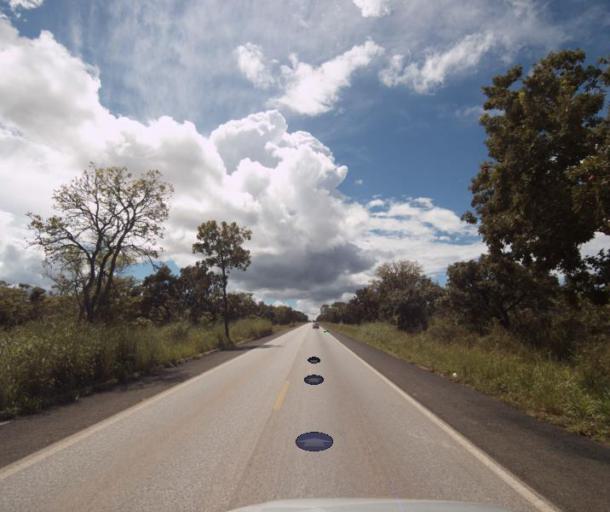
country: BR
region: Goias
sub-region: Uruacu
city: Uruacu
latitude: -14.0358
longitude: -49.0883
